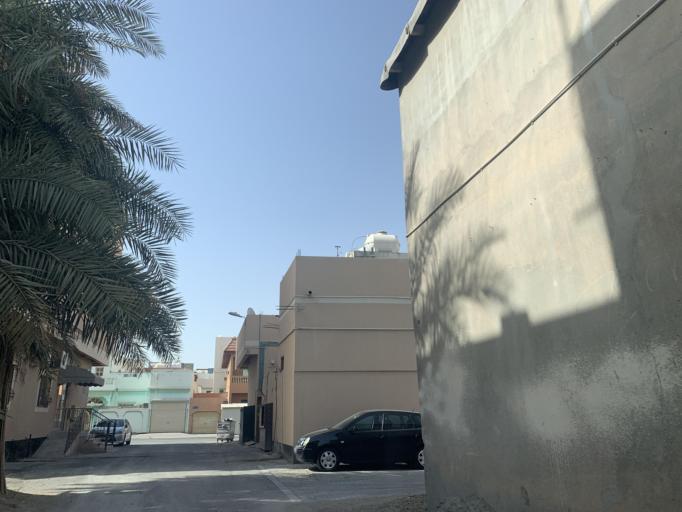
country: BH
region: Northern
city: Sitrah
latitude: 26.1595
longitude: 50.6103
